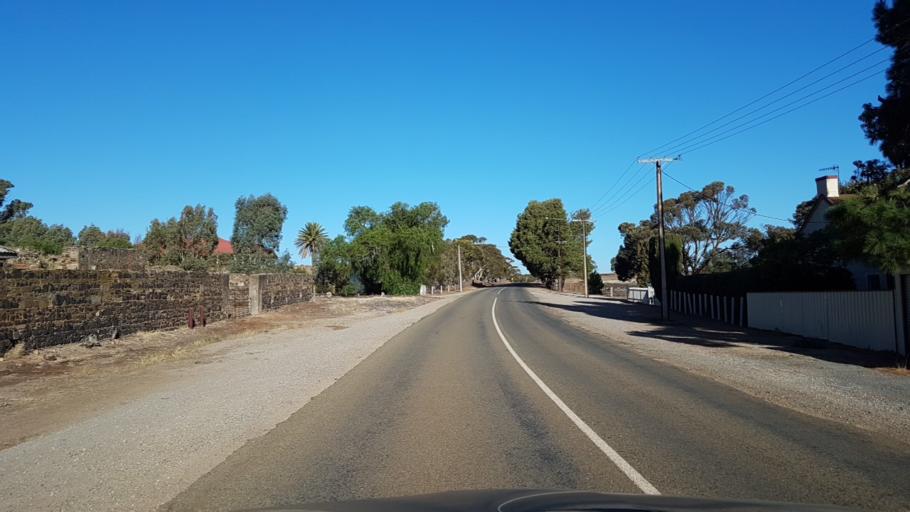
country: AU
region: South Australia
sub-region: Clare and Gilbert Valleys
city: Clare
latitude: -33.6724
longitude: 138.9358
